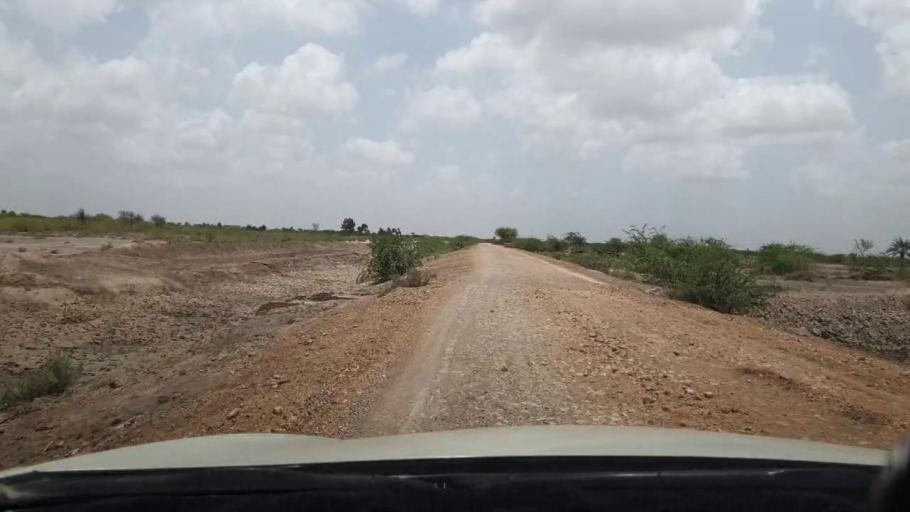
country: PK
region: Sindh
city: Kadhan
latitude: 24.3900
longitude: 68.9343
